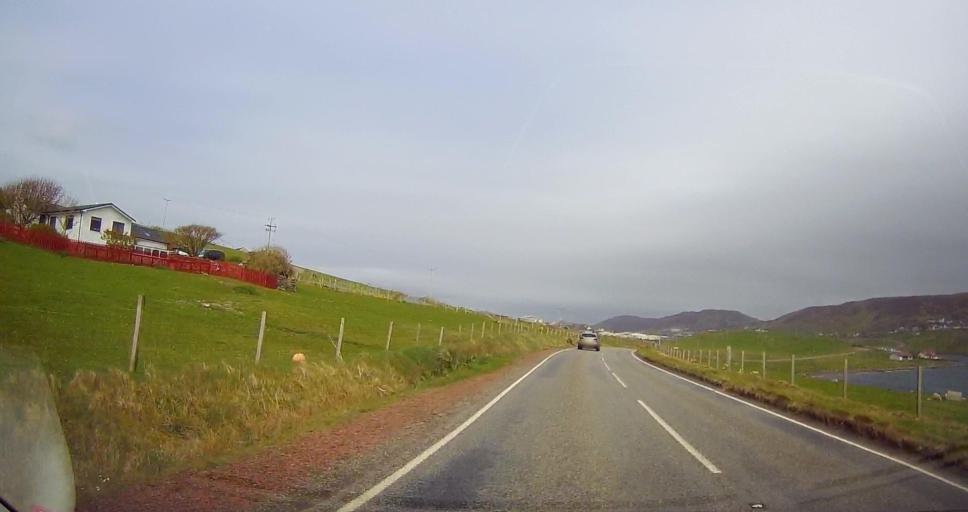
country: GB
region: Scotland
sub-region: Shetland Islands
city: Sandwick
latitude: 60.1236
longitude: -1.2870
